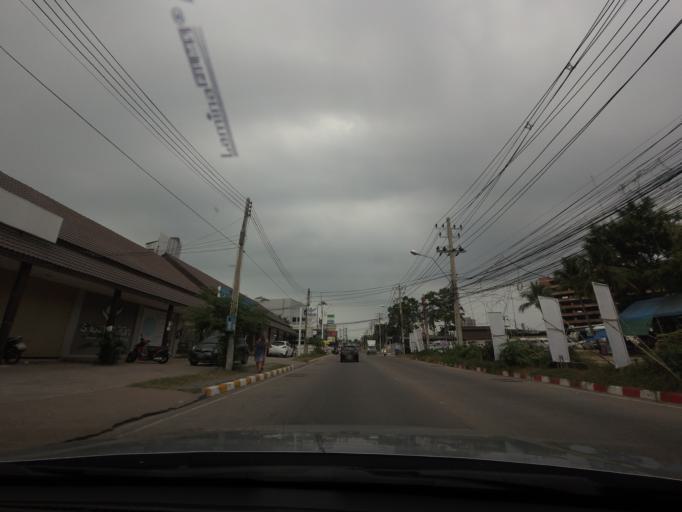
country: TH
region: Chon Buri
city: Phatthaya
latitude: 12.9473
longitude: 100.8917
